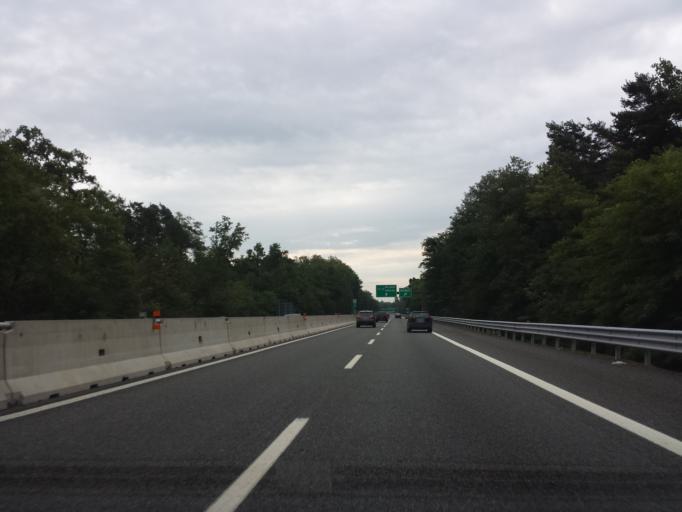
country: IT
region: Lombardy
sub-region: Provincia di Varese
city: Arsago Seprio
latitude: 45.6982
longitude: 8.7463
